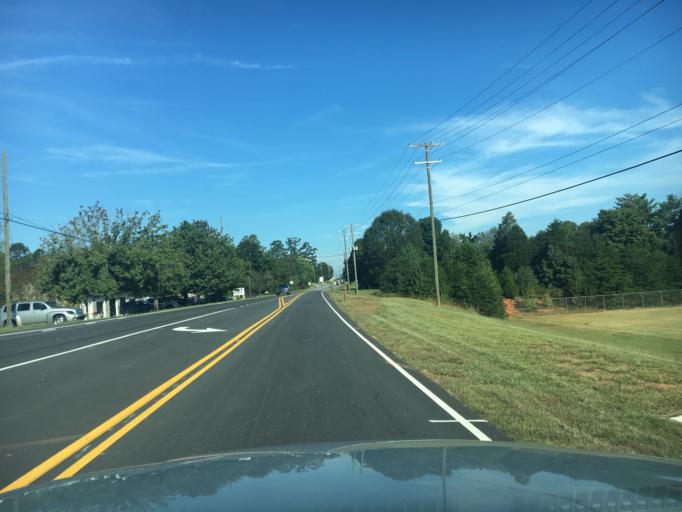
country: US
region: North Carolina
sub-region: Catawba County
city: Hickory
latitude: 35.6975
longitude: -81.2918
